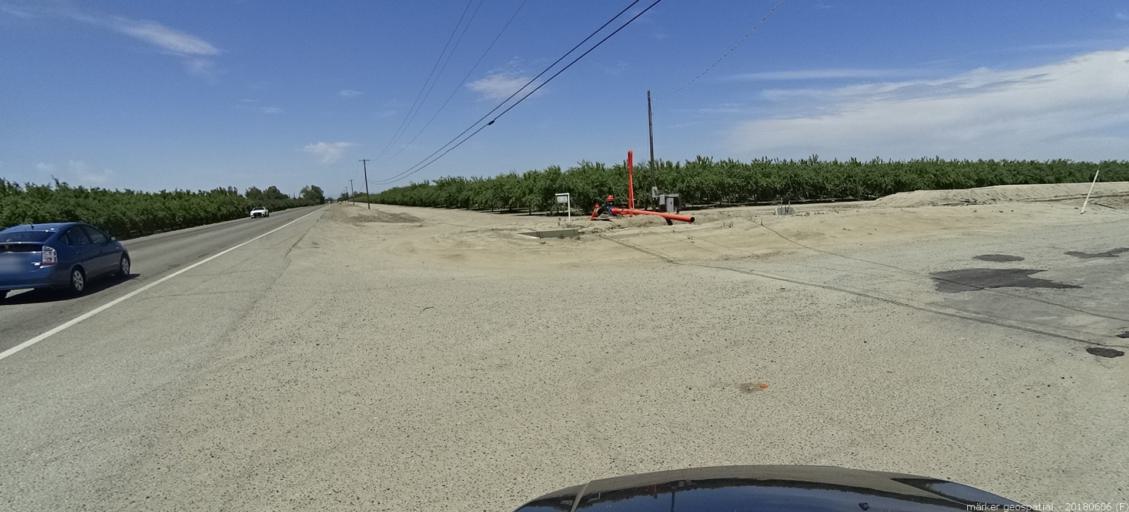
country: US
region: California
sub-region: Fresno County
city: Firebaugh
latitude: 36.8586
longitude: -120.3997
